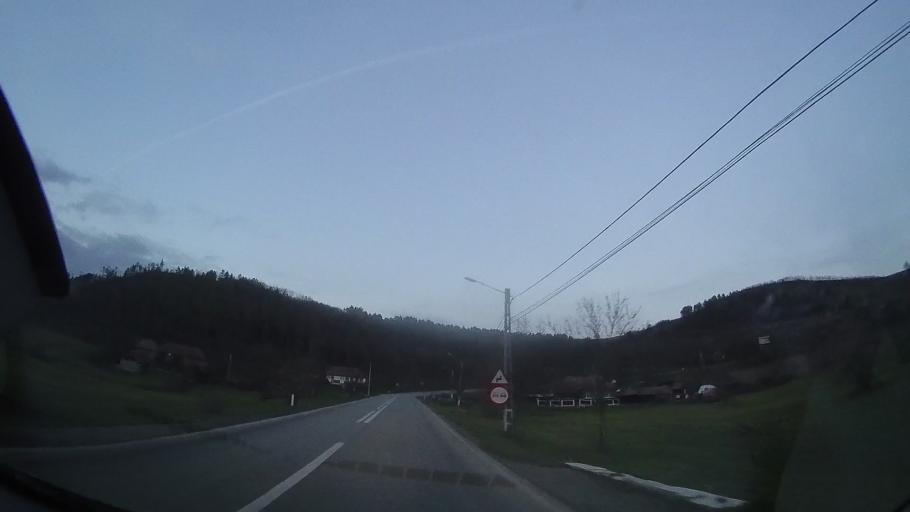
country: RO
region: Cluj
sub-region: Comuna Mociu
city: Mociu
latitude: 46.8028
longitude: 24.0412
